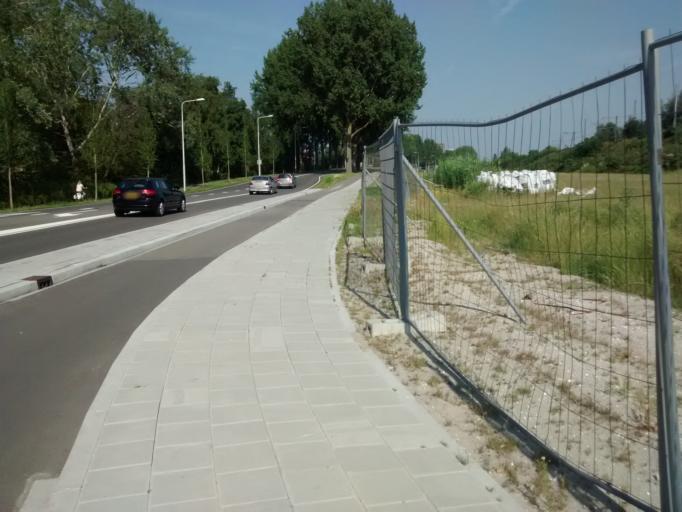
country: NL
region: South Holland
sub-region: Gemeente Gouda
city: Bloemendaal
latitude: 52.0199
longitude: 4.6869
